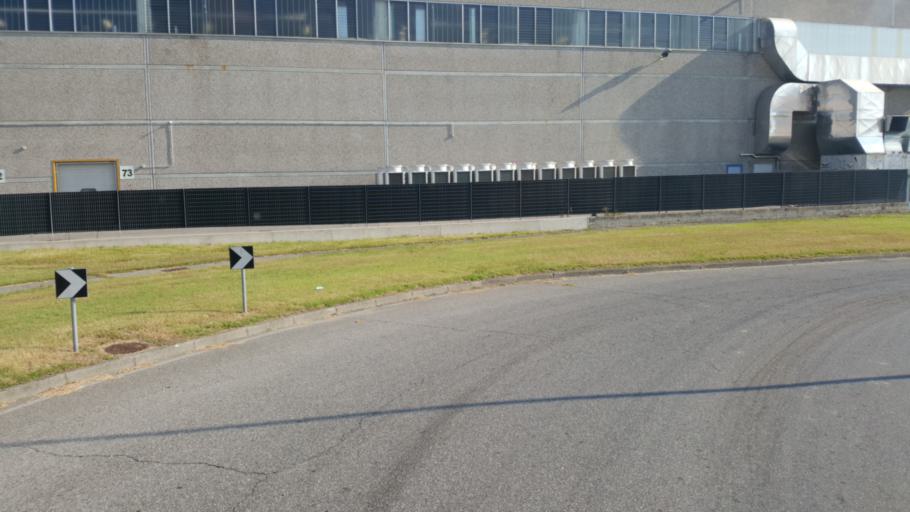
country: IT
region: Lombardy
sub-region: Provincia di Cremona
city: Soresina
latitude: 45.2837
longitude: 9.8721
